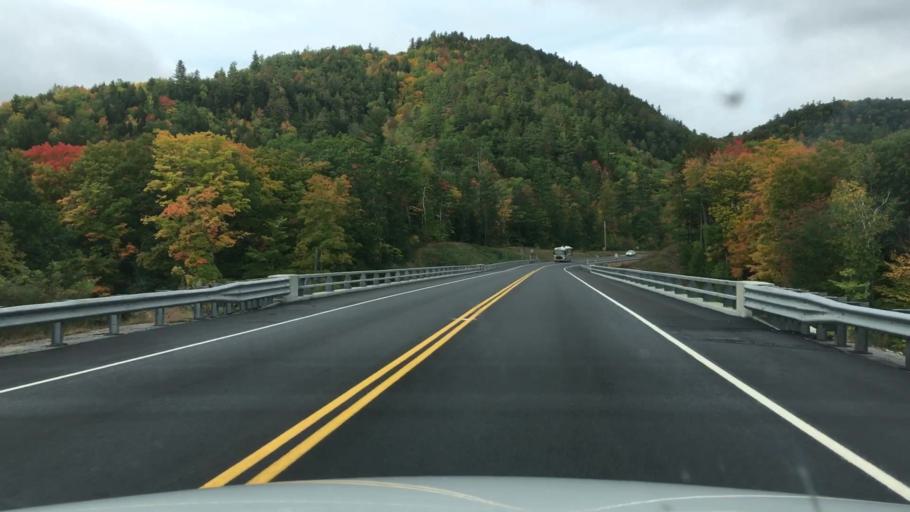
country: US
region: Maine
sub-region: Oxford County
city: Bethel
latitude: 44.3926
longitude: -70.9795
